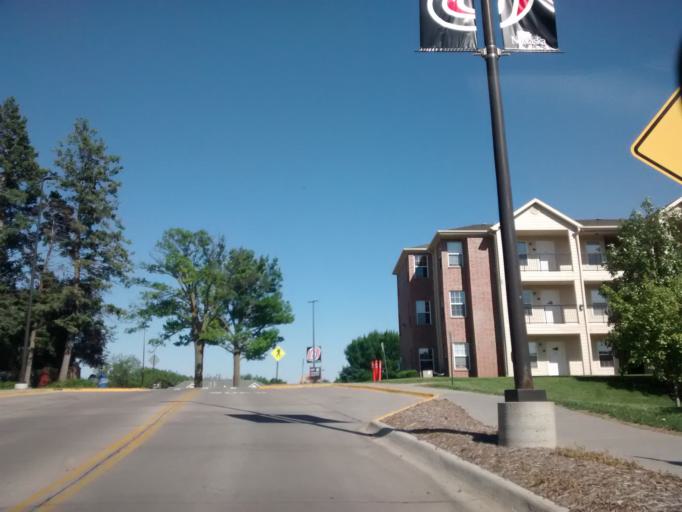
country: US
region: Nebraska
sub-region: Douglas County
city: Ralston
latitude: 41.2574
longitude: -96.0144
